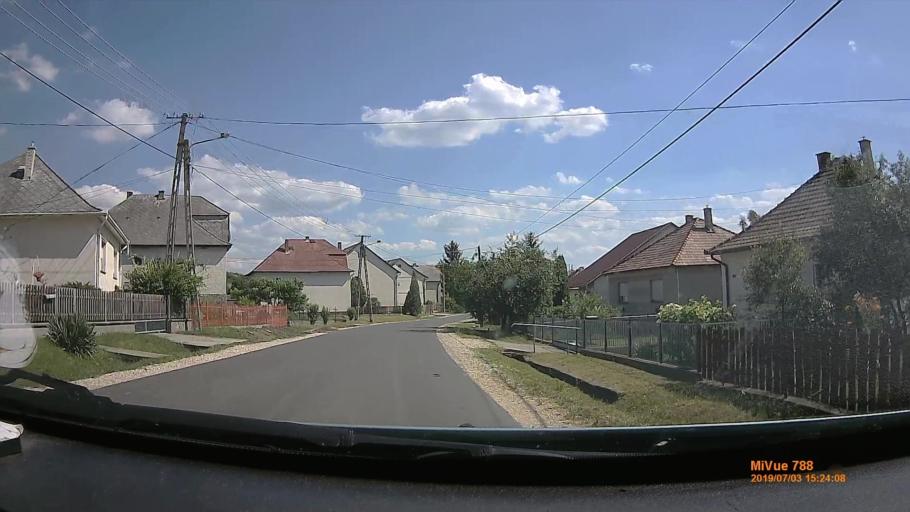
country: HU
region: Borsod-Abauj-Zemplen
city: Farkaslyuk
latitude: 48.1953
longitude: 20.3920
